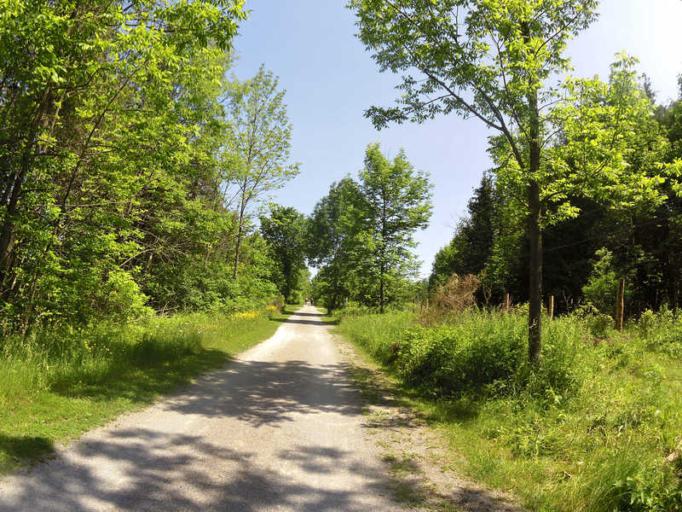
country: CA
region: Ontario
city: Peterborough
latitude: 44.3982
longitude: -78.2631
